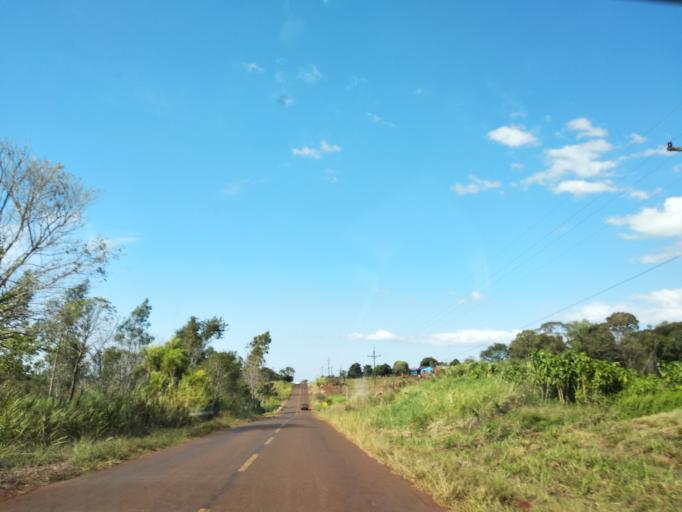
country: PY
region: Itapua
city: Hohenau
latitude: -27.0815
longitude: -55.7075
